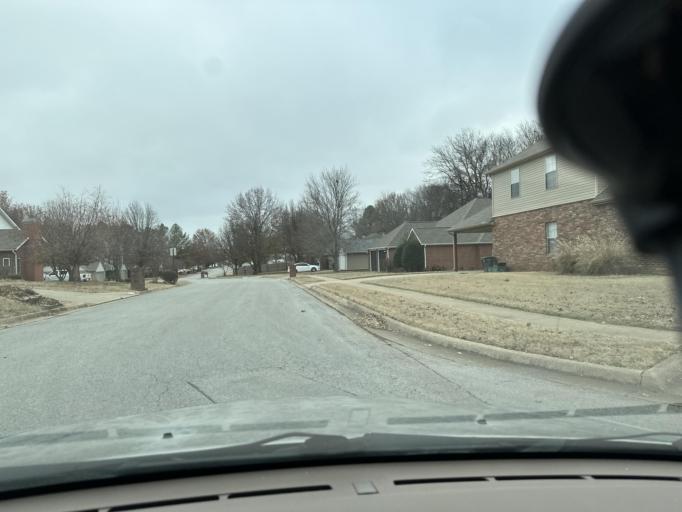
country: US
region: Arkansas
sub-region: Washington County
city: Fayetteville
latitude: 36.0854
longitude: -94.1175
